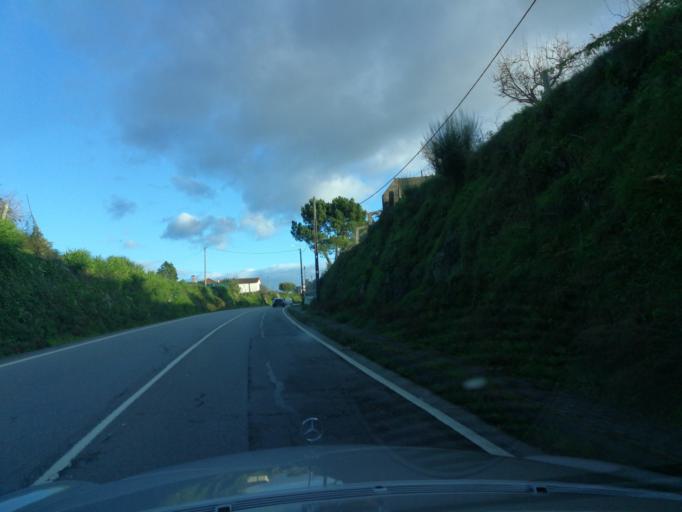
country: PT
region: Braga
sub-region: Esposende
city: Marinhas
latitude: 41.6156
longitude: -8.7478
